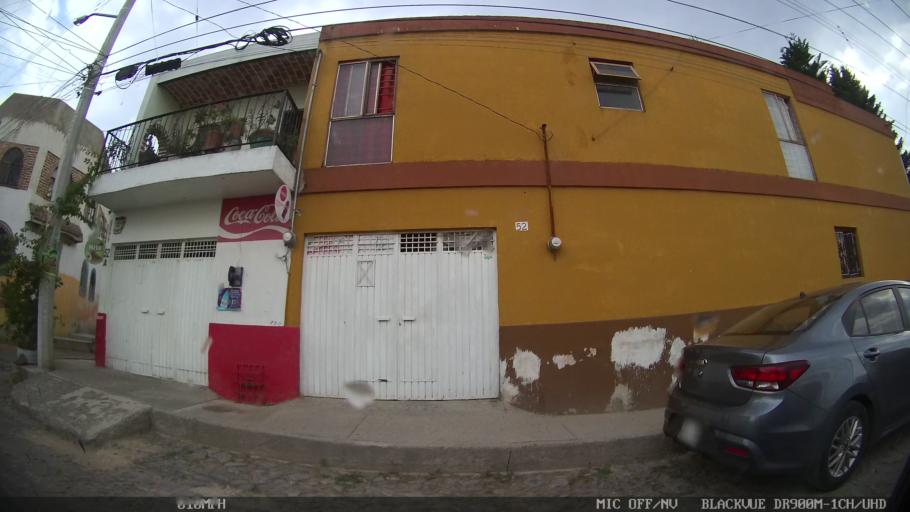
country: MX
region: Jalisco
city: Tonala
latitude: 20.6195
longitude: -103.2666
